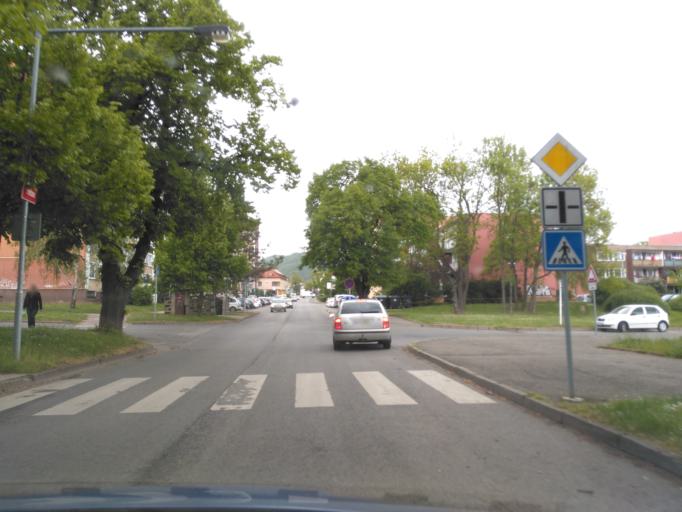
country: CZ
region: Central Bohemia
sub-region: Okres Beroun
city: Beroun
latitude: 49.9604
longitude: 14.0714
